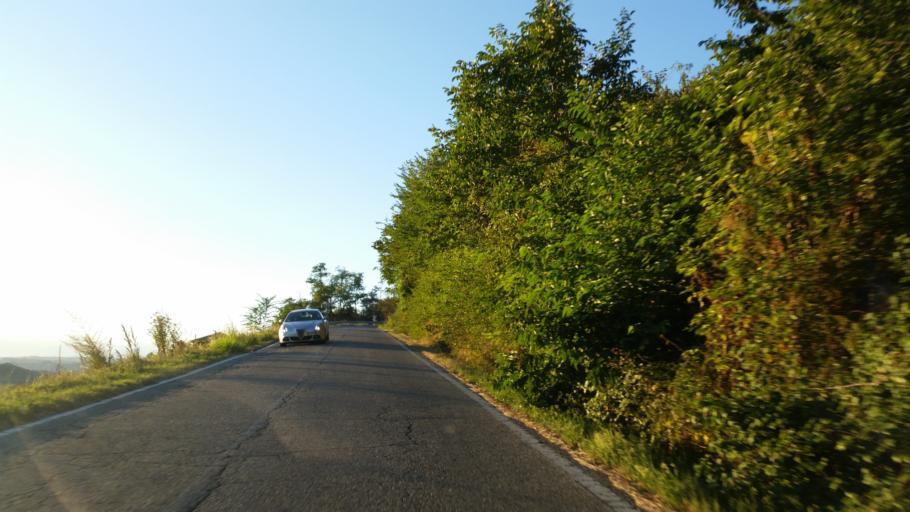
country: IT
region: Piedmont
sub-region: Provincia di Cuneo
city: Mango
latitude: 44.6960
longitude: 8.1390
